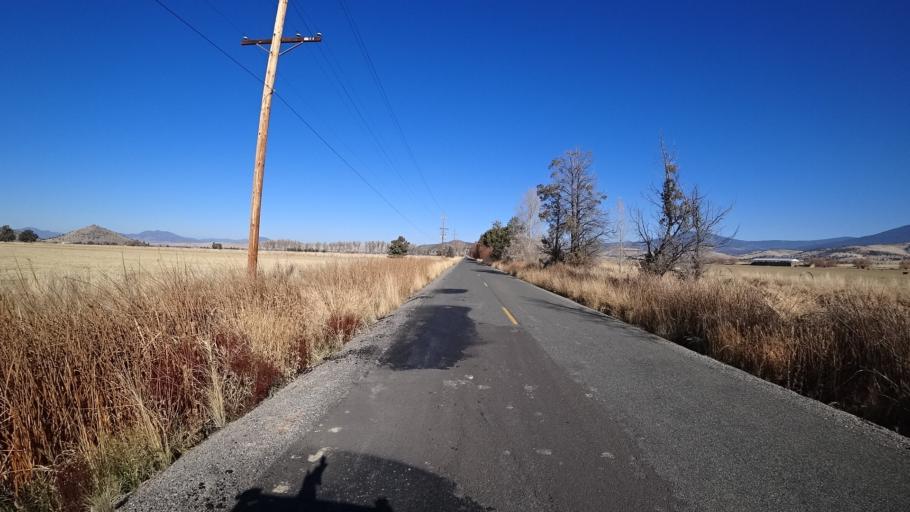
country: US
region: California
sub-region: Siskiyou County
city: Montague
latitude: 41.6763
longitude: -122.3699
